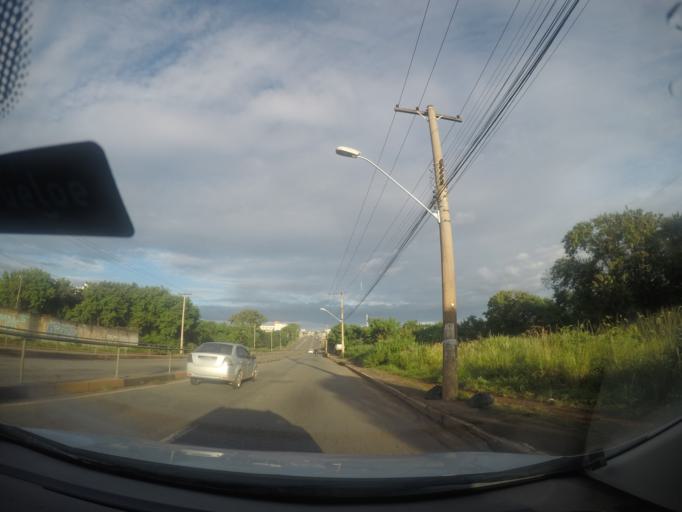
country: BR
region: Goias
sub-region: Goiania
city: Goiania
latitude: -16.6656
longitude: -49.3151
